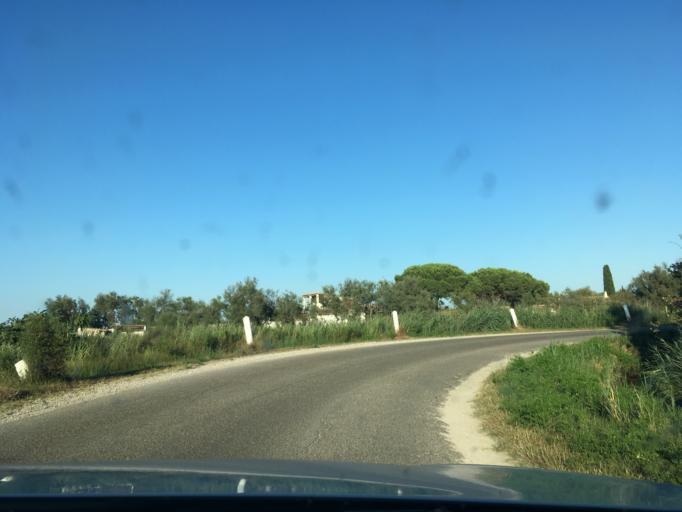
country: FR
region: Provence-Alpes-Cote d'Azur
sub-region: Departement des Bouches-du-Rhone
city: Saintes-Maries-de-la-Mer
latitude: 43.4820
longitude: 4.4015
